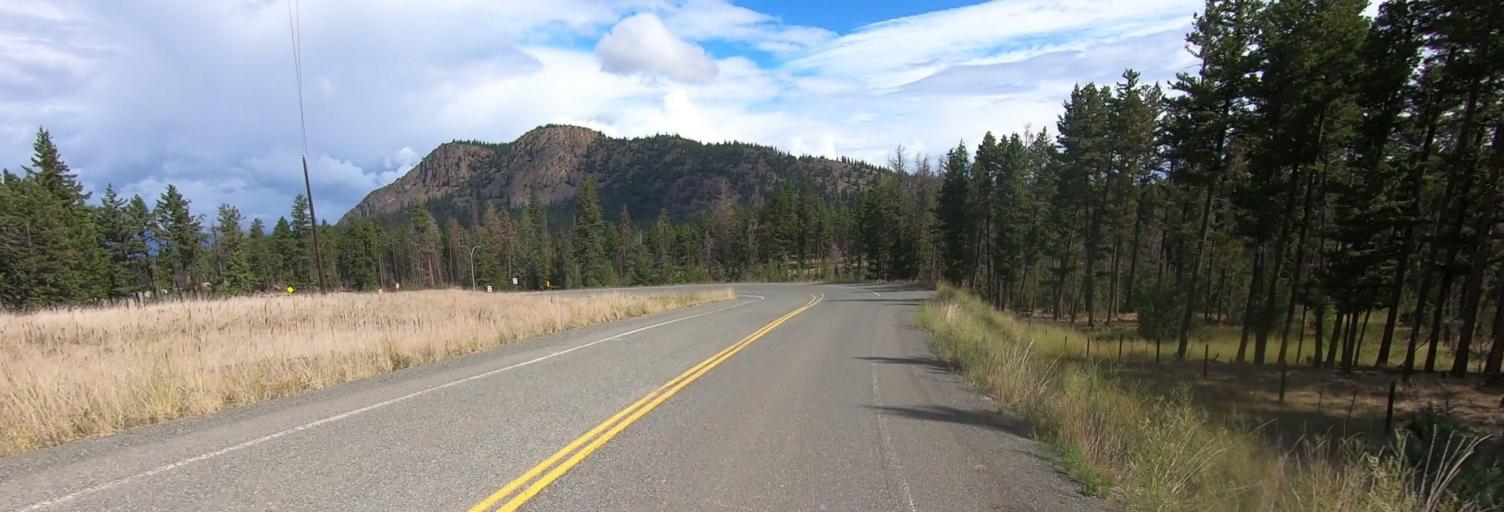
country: CA
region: British Columbia
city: Kamloops
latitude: 50.6196
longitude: -120.4705
